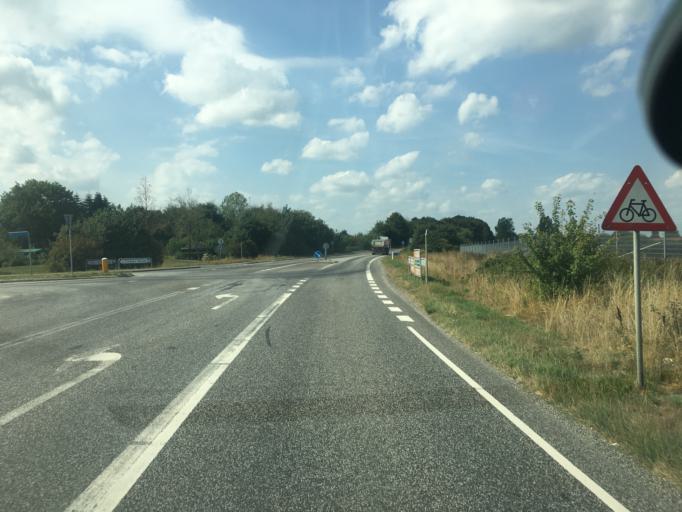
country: DK
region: South Denmark
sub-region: Aabenraa Kommune
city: Tinglev
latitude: 54.9414
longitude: 9.2649
